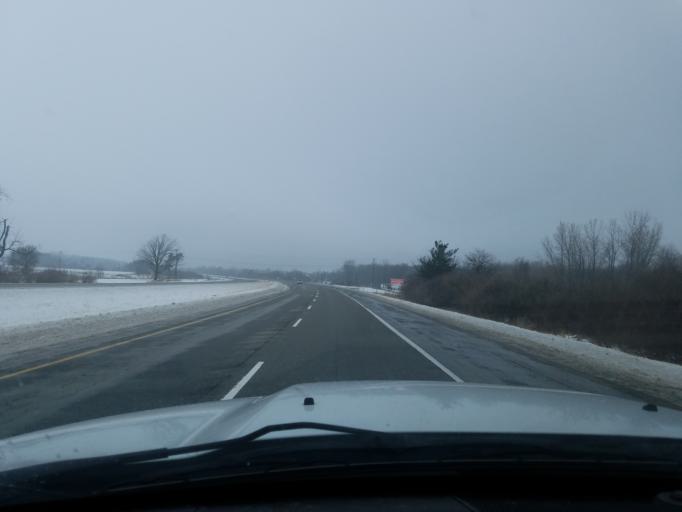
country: US
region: Indiana
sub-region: Fulton County
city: Rochester
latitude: 41.0083
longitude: -86.1676
